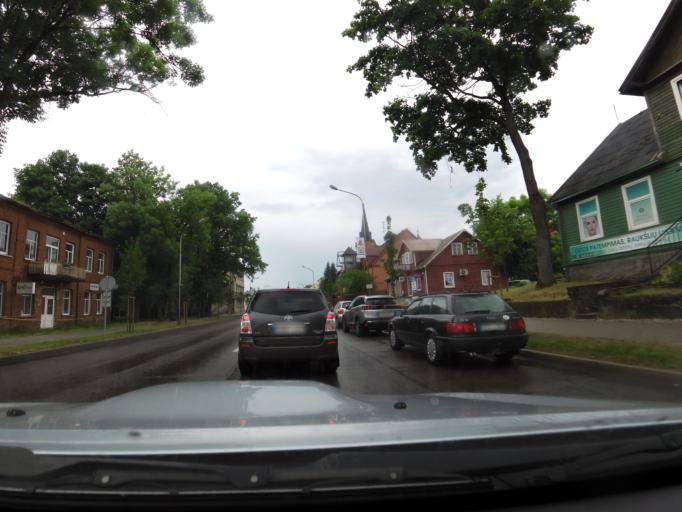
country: LT
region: Marijampoles apskritis
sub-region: Marijampole Municipality
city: Marijampole
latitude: 54.5507
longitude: 23.3482
